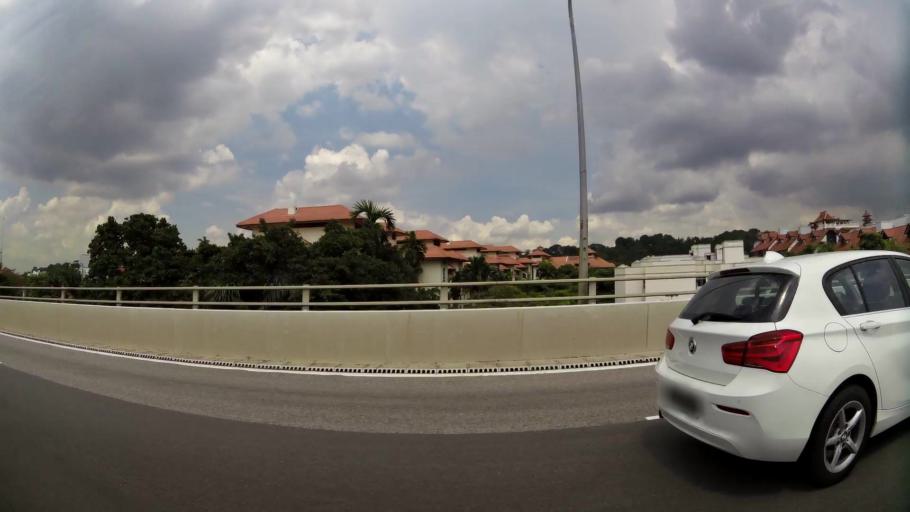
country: SG
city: Singapore
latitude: 1.2781
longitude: 103.7868
